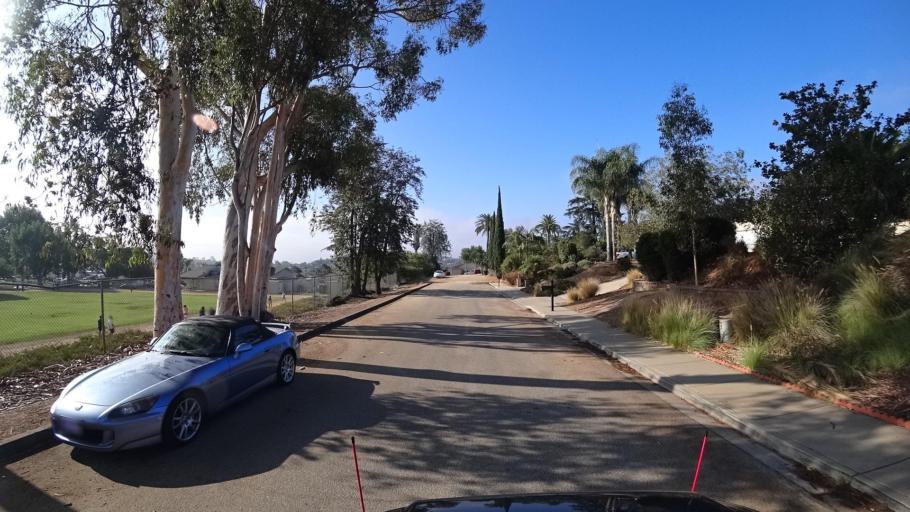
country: US
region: California
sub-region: San Diego County
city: Fallbrook
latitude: 33.3779
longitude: -117.2569
